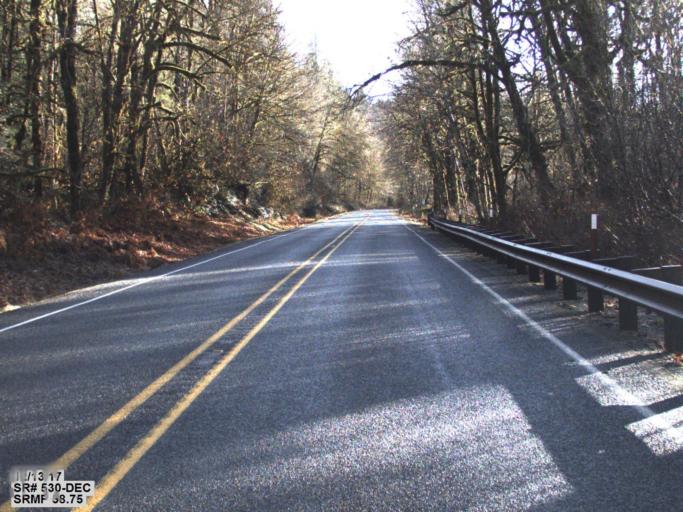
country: US
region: Washington
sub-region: Snohomish County
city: Darrington
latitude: 48.3747
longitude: -121.5456
